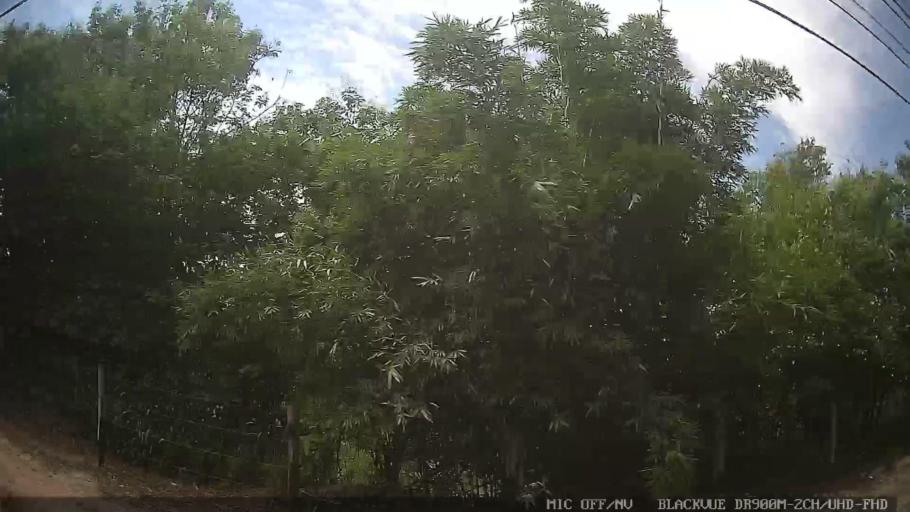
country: BR
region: Sao Paulo
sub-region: Santa Isabel
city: Santa Isabel
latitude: -23.4160
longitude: -46.2089
